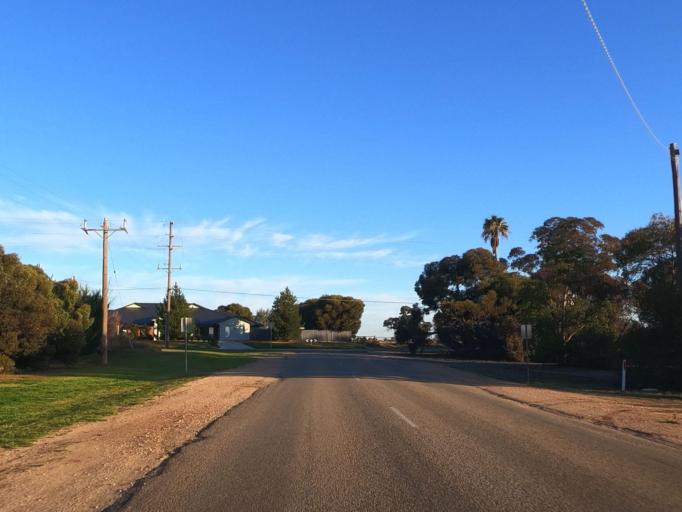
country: AU
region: Victoria
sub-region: Swan Hill
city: Swan Hill
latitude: -35.3599
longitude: 143.5518
